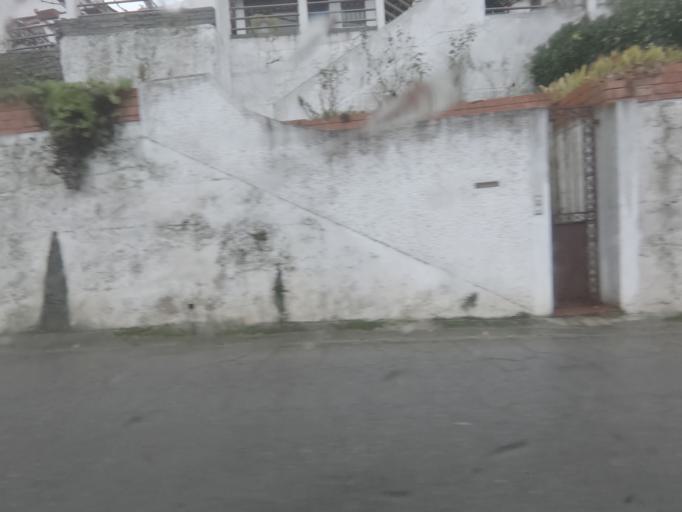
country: PT
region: Vila Real
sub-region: Peso da Regua
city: Peso da Regua
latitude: 41.1695
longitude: -7.7662
